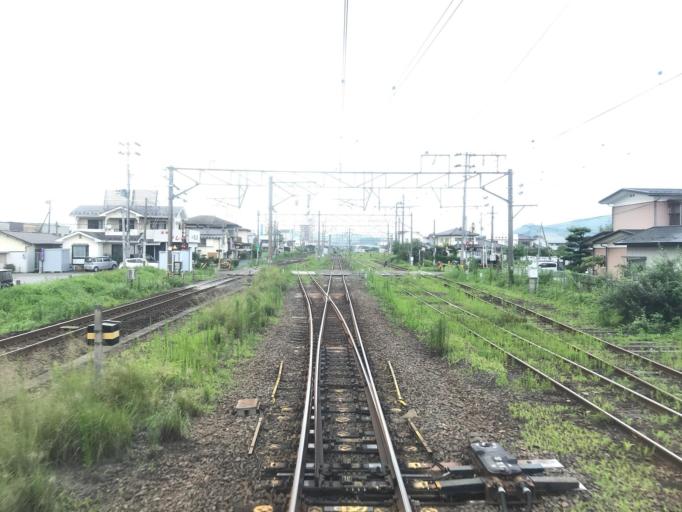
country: JP
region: Miyagi
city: Shiroishi
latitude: 37.9994
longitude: 140.6256
